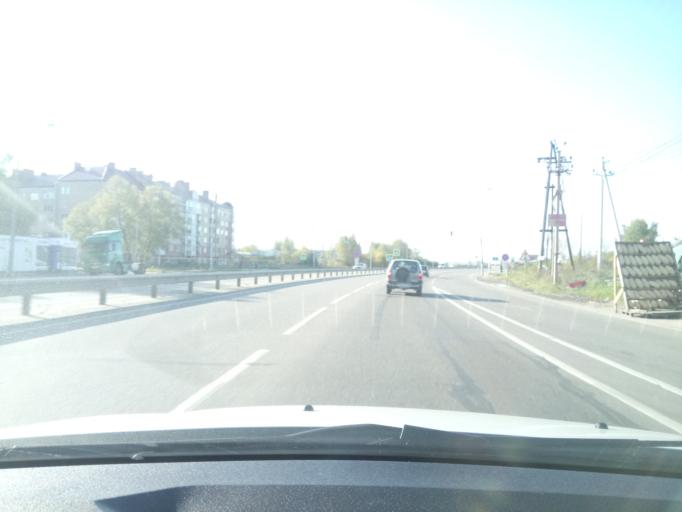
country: RU
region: Nizjnij Novgorod
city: Burevestnik
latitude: 56.1639
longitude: 43.9161
